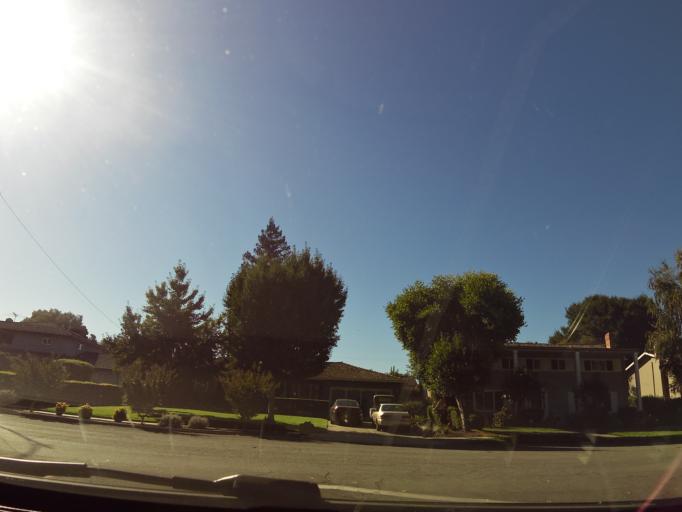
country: US
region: California
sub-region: Santa Clara County
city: Buena Vista
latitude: 37.2906
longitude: -121.9193
